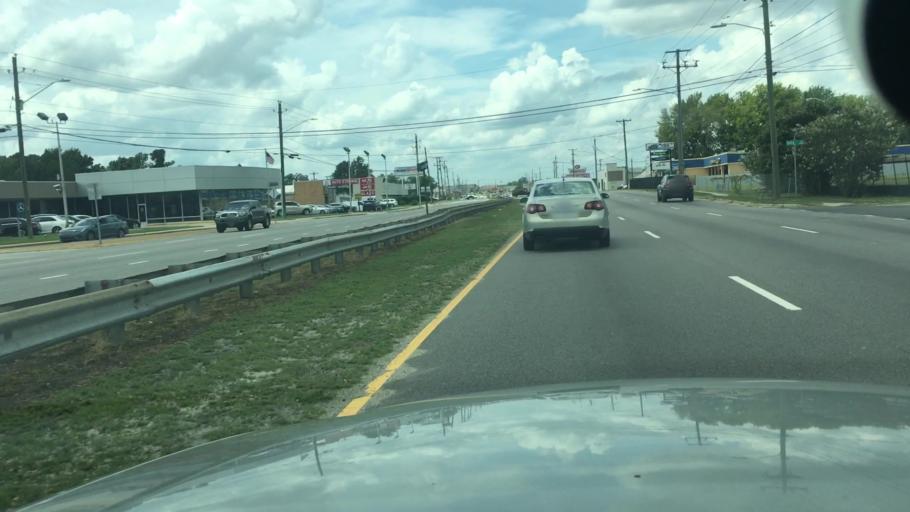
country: US
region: North Carolina
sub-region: Cumberland County
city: Fayetteville
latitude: 35.0756
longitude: -78.9315
